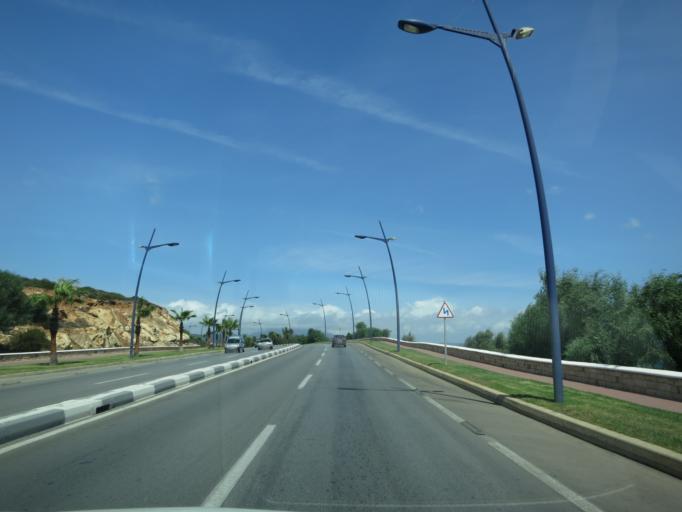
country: ES
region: Ceuta
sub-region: Ceuta
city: Ceuta
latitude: 35.7813
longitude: -5.3491
